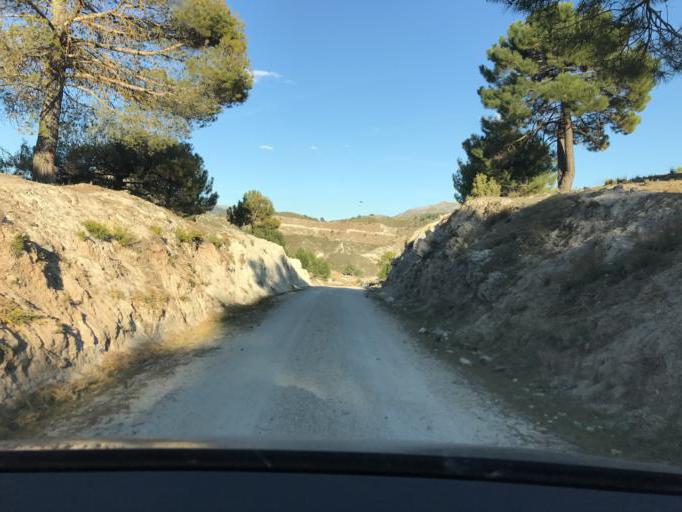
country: ES
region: Andalusia
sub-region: Provincia de Granada
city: Quentar
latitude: 37.2339
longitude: -3.4136
